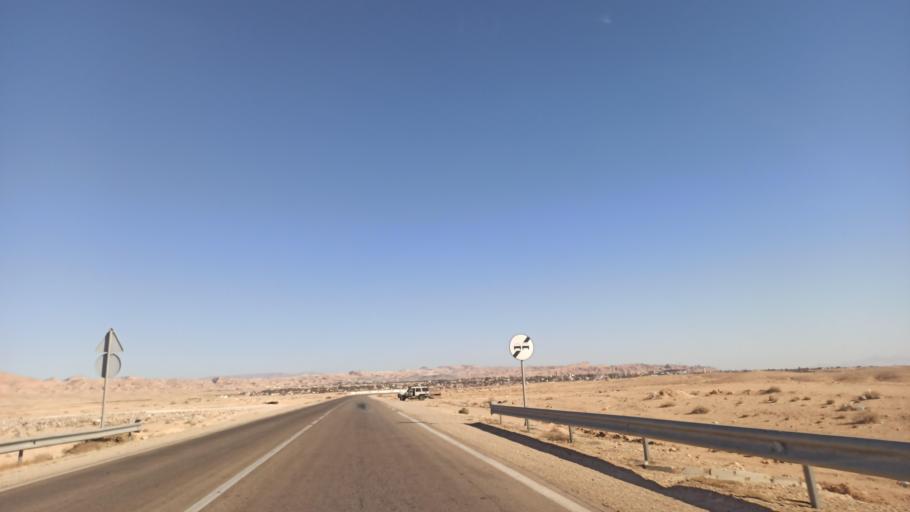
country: TN
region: Gafsa
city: Al Metlaoui
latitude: 34.3033
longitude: 8.3620
